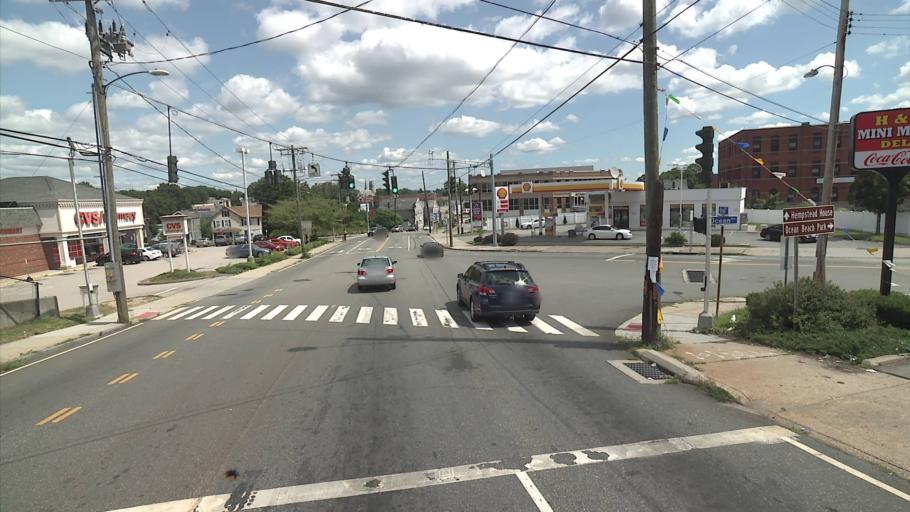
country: US
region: Connecticut
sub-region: New London County
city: New London
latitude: 41.3485
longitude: -72.1074
